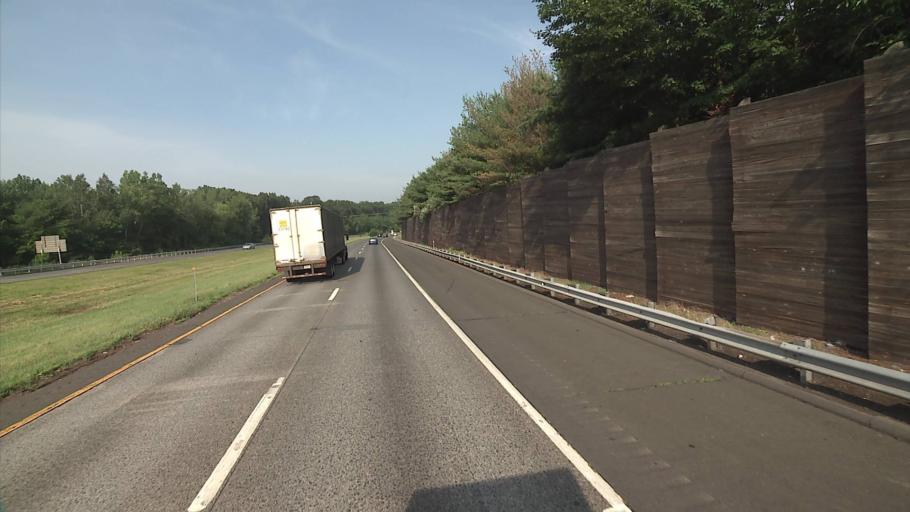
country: US
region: Connecticut
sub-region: New Haven County
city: Meriden
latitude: 41.5539
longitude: -72.8551
